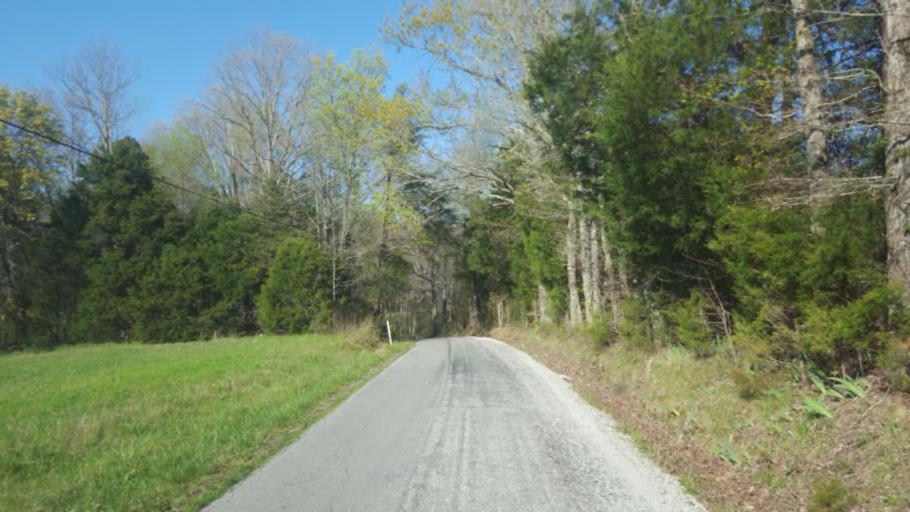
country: US
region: Kentucky
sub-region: Barren County
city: Cave City
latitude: 37.1728
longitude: -86.0349
